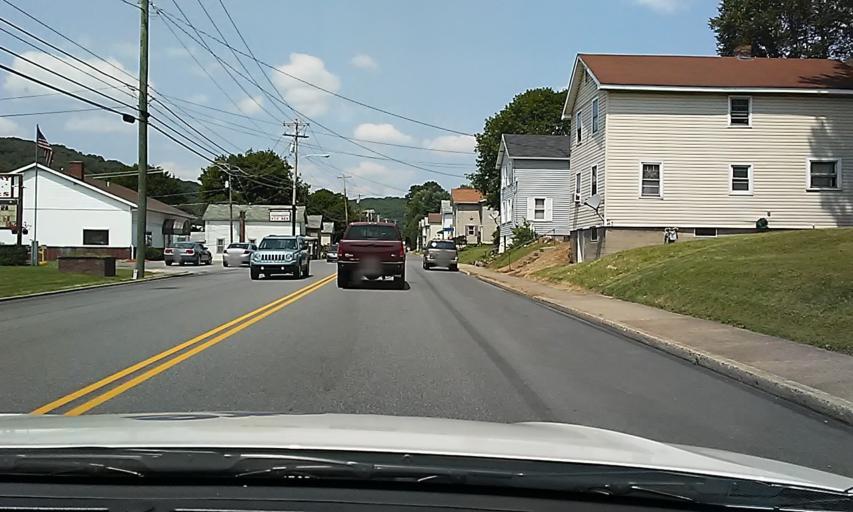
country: US
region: Pennsylvania
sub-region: Elk County
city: Ridgway
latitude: 41.4282
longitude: -78.7331
